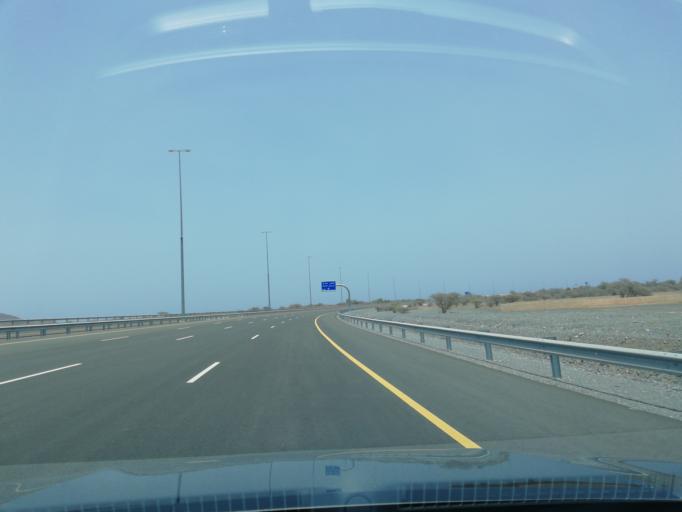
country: AE
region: Al Fujayrah
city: Al Fujayrah
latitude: 24.9471
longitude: 56.3592
